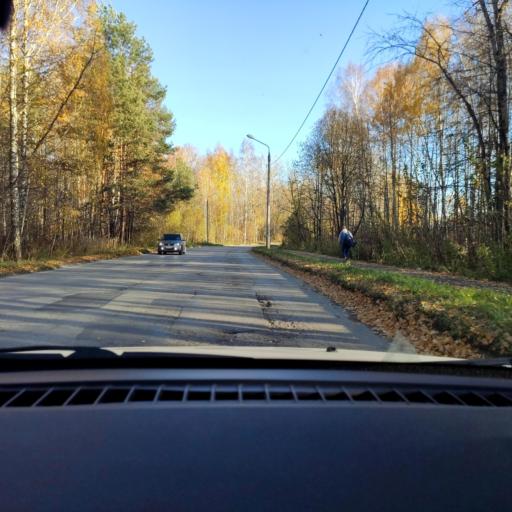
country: RU
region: Perm
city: Perm
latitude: 58.0812
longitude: 56.3636
